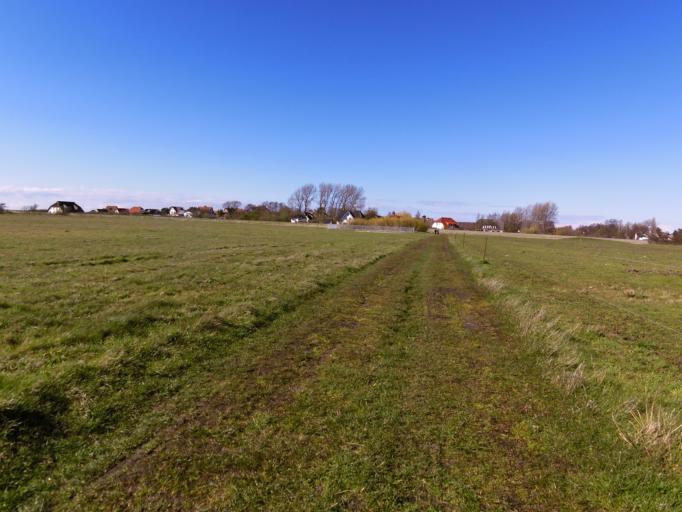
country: DE
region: Mecklenburg-Vorpommern
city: Hiddensee
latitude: 54.5585
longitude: 13.1041
